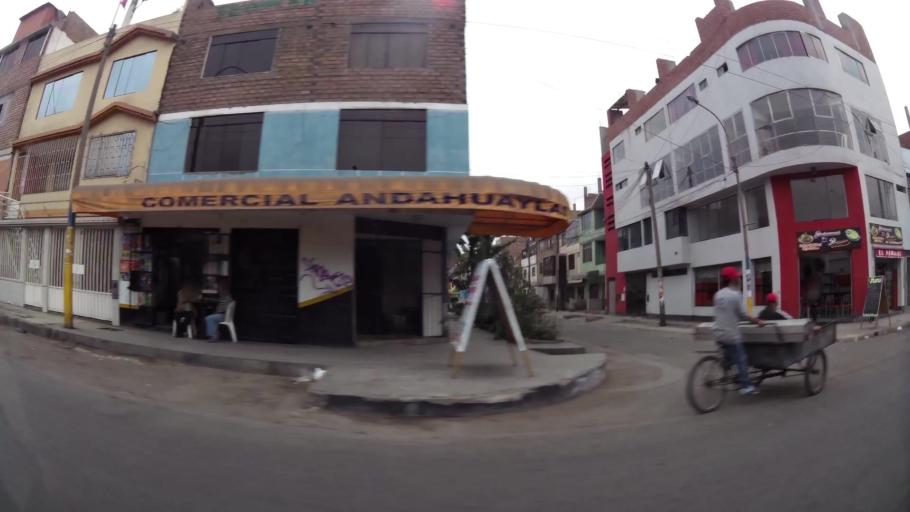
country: PE
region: Lima
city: Lima
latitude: -12.0128
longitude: -77.0074
